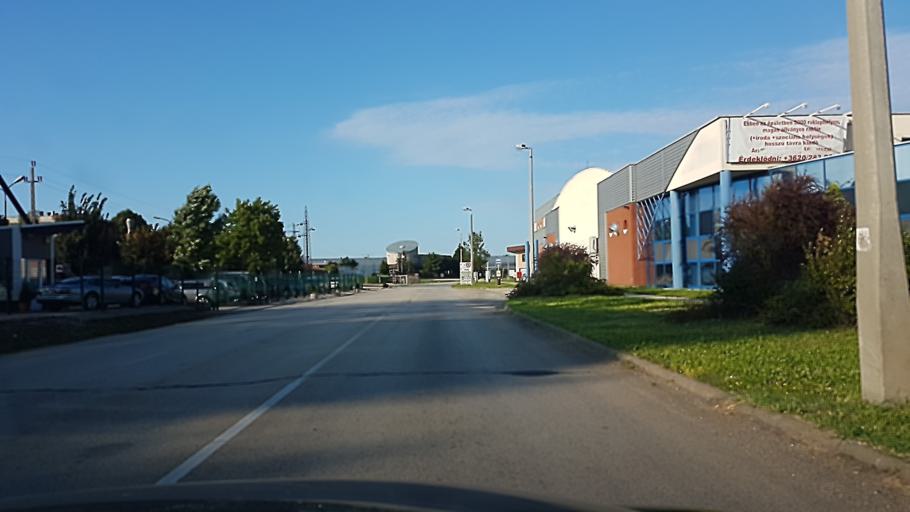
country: HU
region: Fejer
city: Szekesfehervar
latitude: 47.1805
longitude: 18.4746
